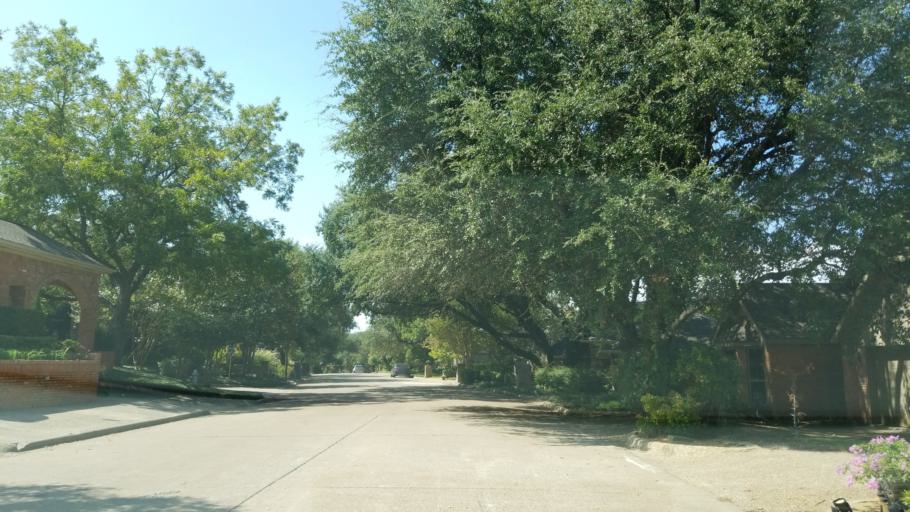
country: US
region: Texas
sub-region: Dallas County
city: Addison
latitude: 32.9680
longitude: -96.8060
